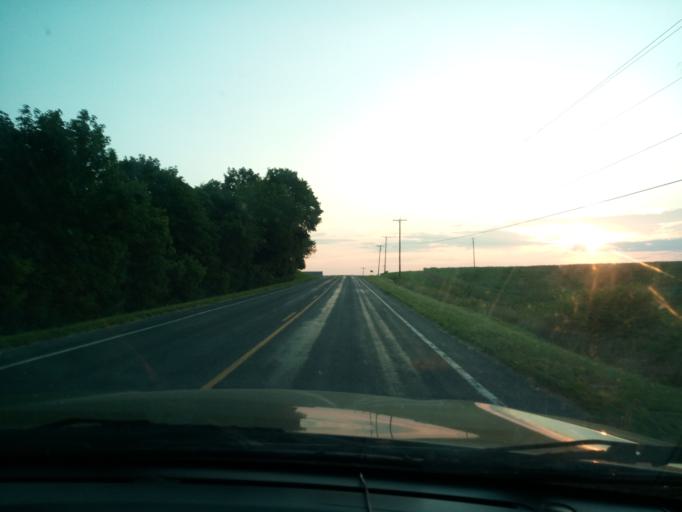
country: US
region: New York
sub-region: Seneca County
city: Bridgeport
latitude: 43.0220
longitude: -76.7734
